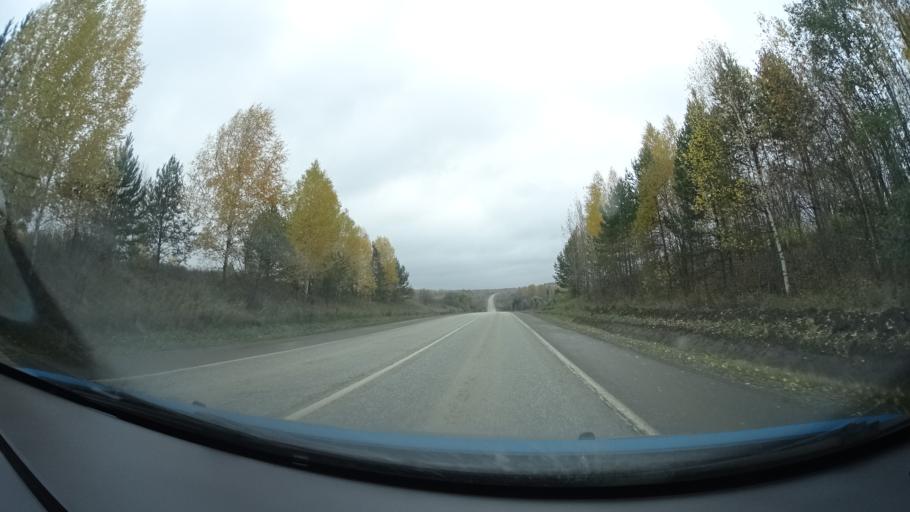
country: RU
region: Perm
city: Osa
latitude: 57.1517
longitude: 55.5293
